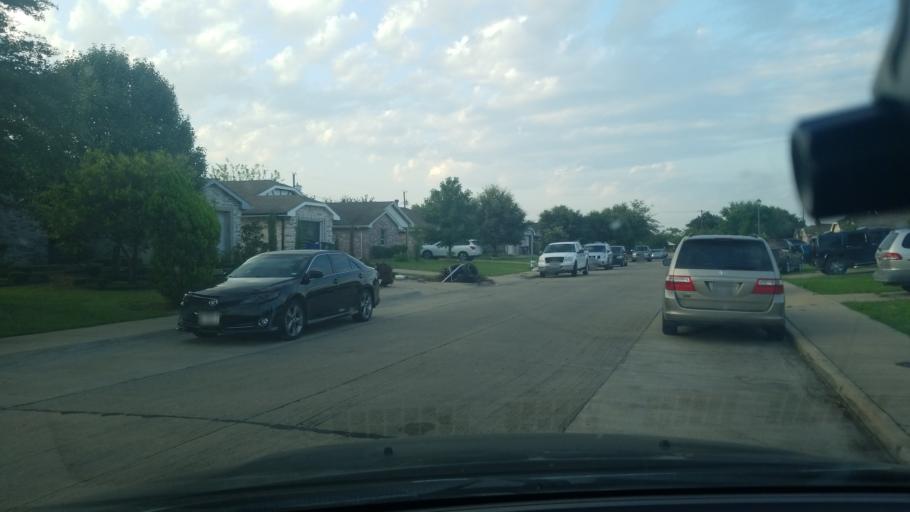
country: US
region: Texas
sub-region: Dallas County
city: Balch Springs
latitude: 32.7295
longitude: -96.6511
